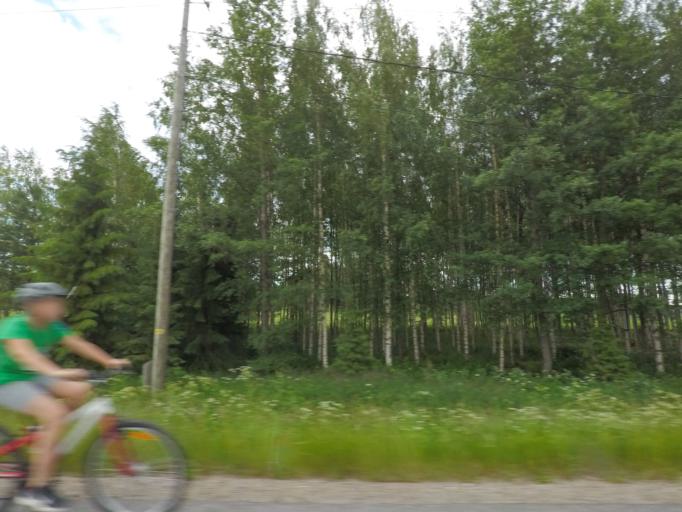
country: FI
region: Uusimaa
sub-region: Porvoo
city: Pukkila
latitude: 60.7561
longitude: 25.4359
